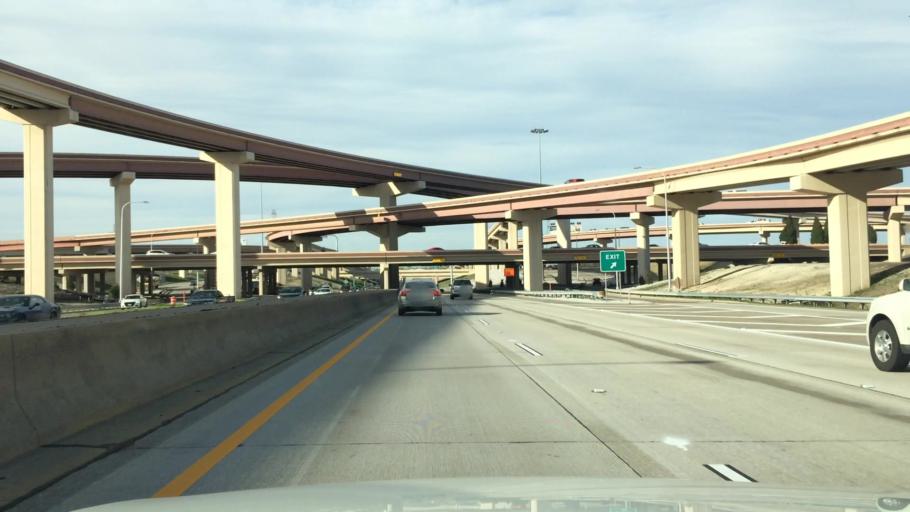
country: US
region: Texas
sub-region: Dallas County
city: Addison
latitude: 33.0113
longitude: -96.8291
